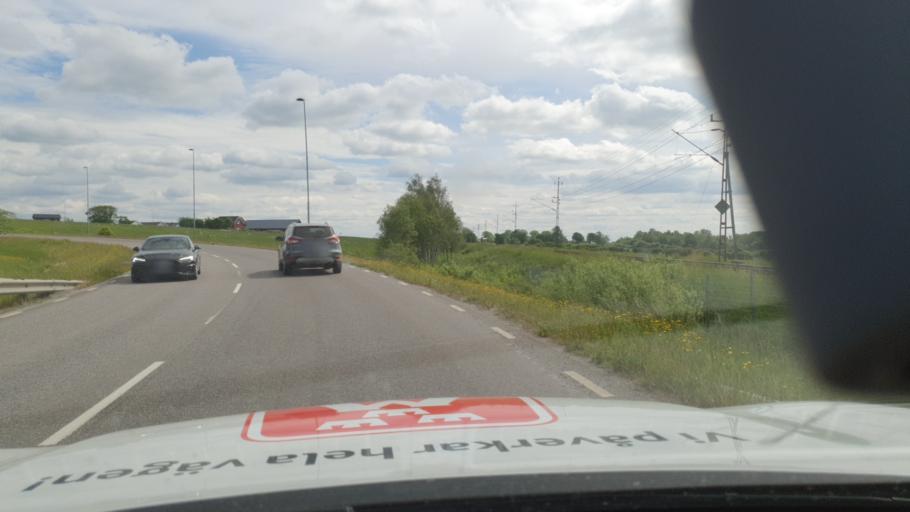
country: SE
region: Vaestra Goetaland
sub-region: Falkopings Kommun
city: Falkoeping
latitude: 58.1537
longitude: 13.5460
